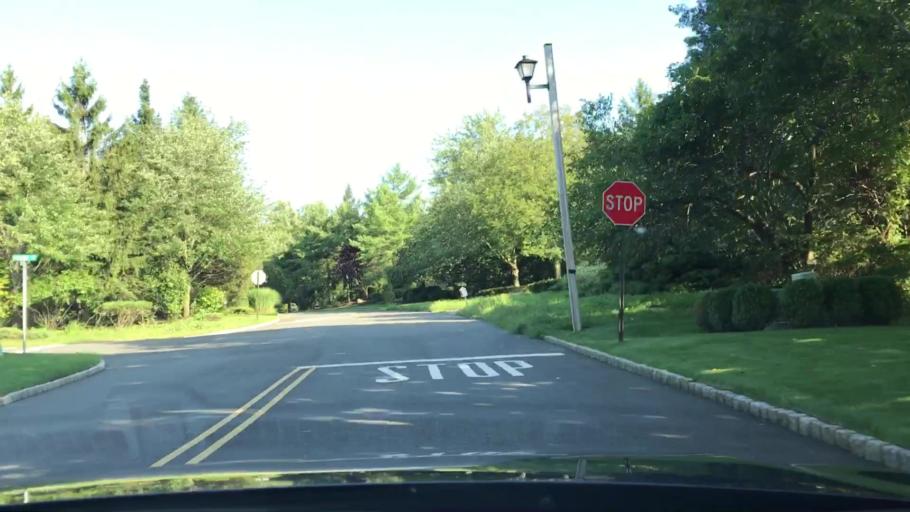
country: US
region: New Jersey
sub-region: Bergen County
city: Cresskill
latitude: 40.9313
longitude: -73.9498
